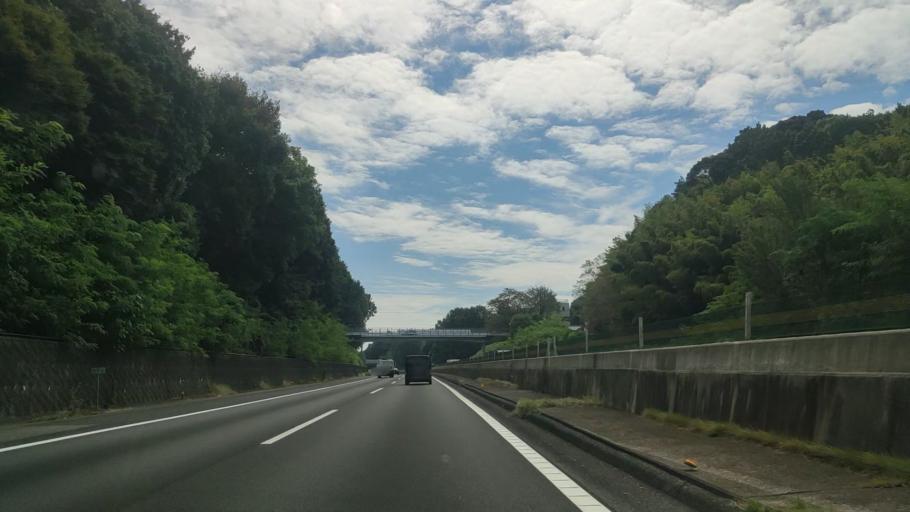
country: JP
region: Aichi
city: Okazaki
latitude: 35.0061
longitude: 137.1754
